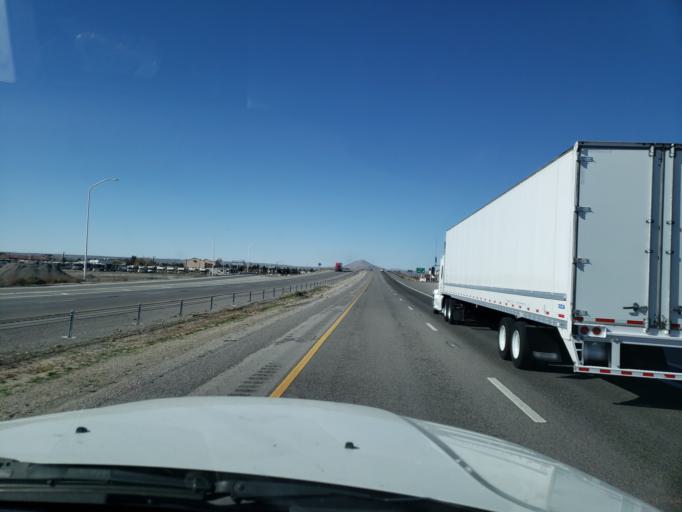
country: US
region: New Mexico
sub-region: Dona Ana County
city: Mesilla
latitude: 32.2877
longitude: -106.7865
